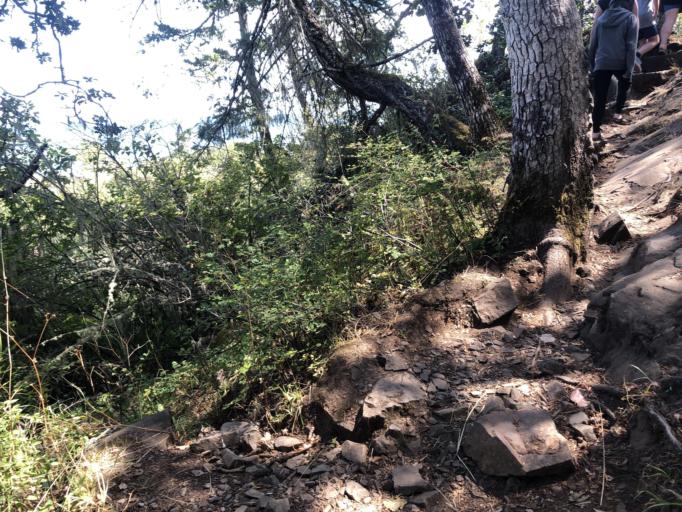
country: CA
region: British Columbia
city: Metchosin
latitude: 48.3628
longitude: -123.5349
